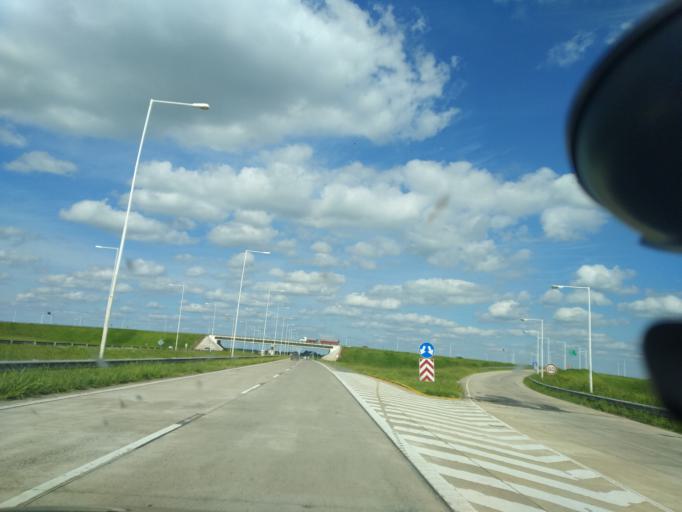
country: AR
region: Santa Fe
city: Carcarana
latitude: -32.8688
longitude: -61.2553
